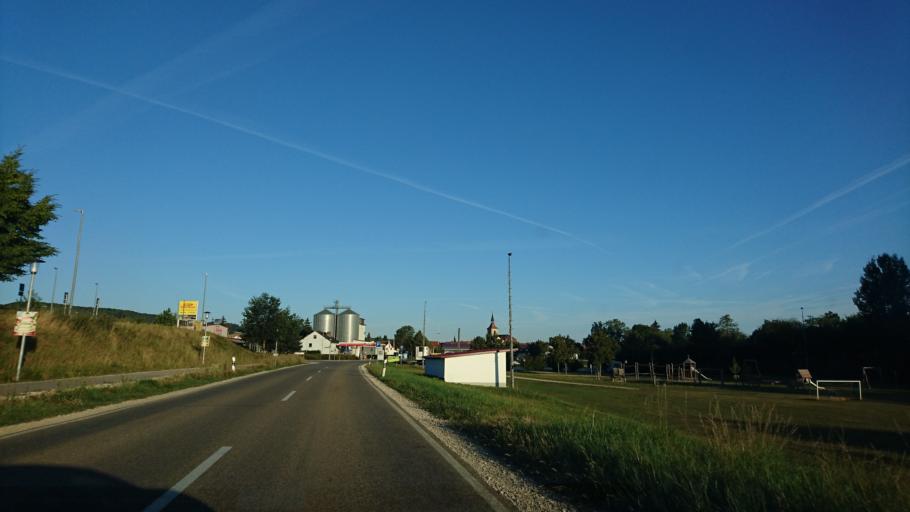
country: DE
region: Bavaria
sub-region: Regierungsbezirk Mittelfranken
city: Thalmassing
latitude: 49.0867
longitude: 11.2285
